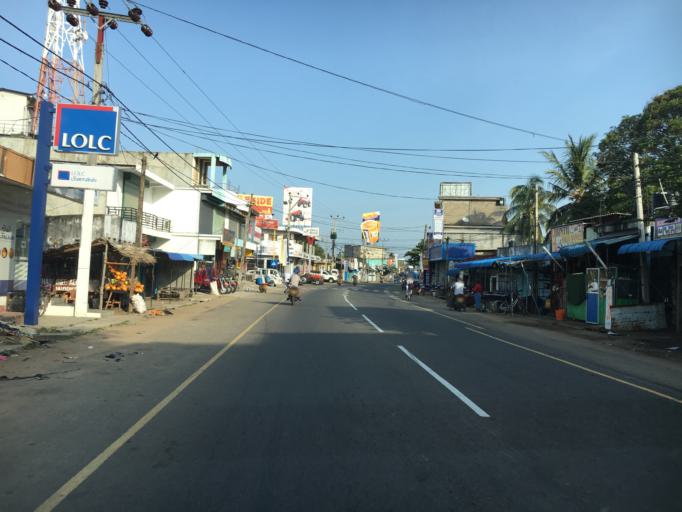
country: LK
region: Eastern Province
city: Eravur Town
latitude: 7.9142
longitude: 81.5233
